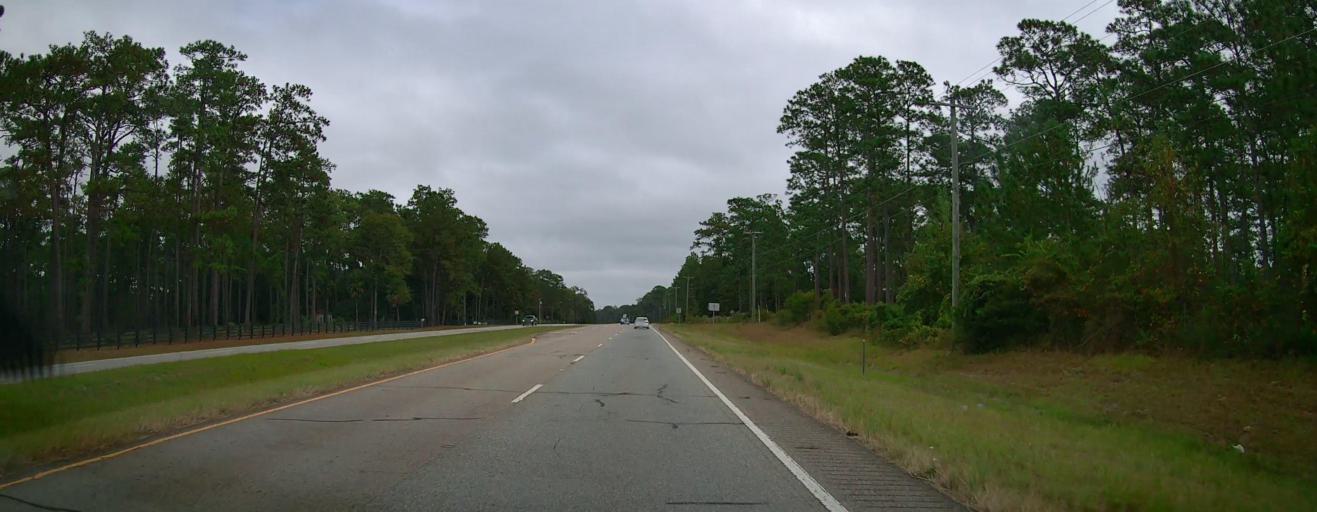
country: US
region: Georgia
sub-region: Thomas County
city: Thomasville
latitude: 30.7871
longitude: -84.0415
